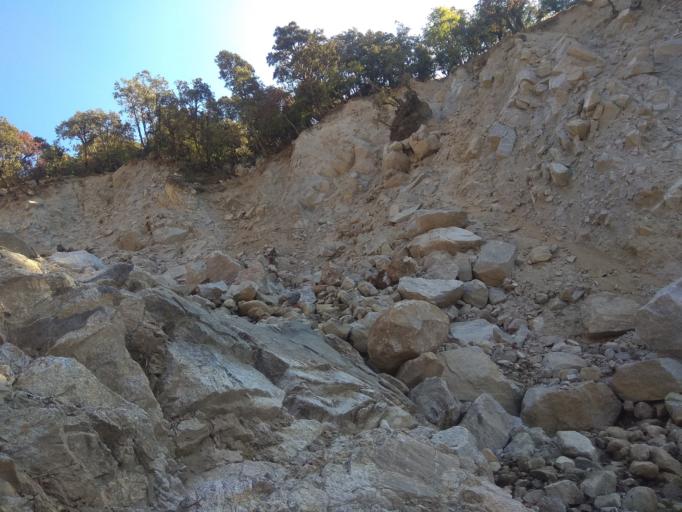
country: NP
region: Far Western
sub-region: Seti Zone
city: Achham
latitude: 29.2740
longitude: 81.6137
